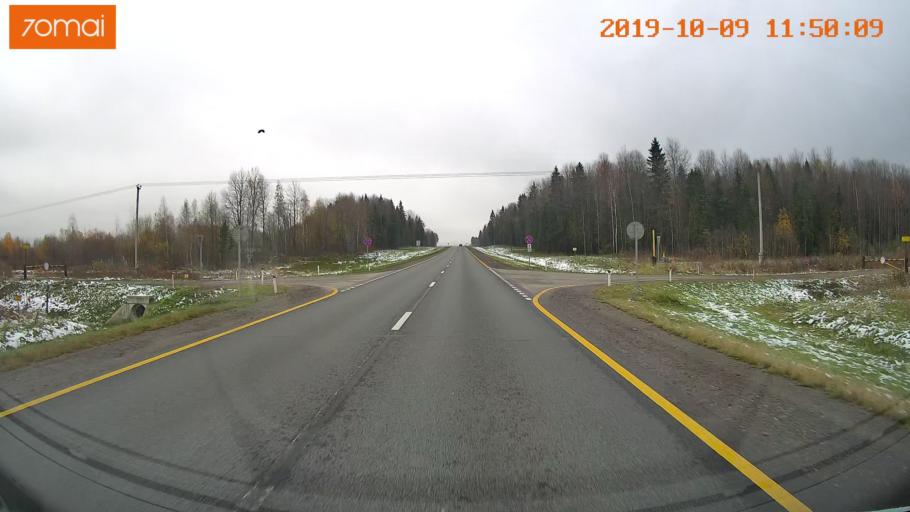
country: RU
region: Vologda
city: Gryazovets
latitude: 58.8092
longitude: 40.2418
